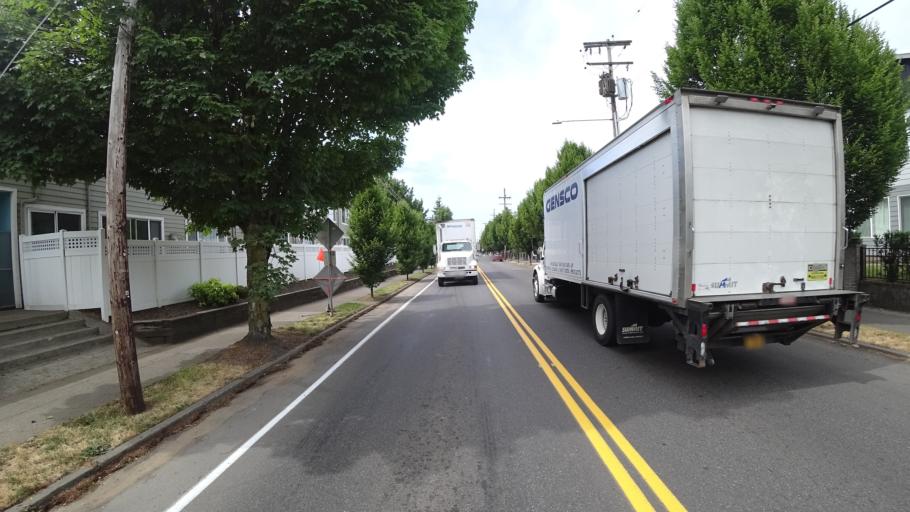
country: US
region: Oregon
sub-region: Washington County
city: West Haven
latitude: 45.5935
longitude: -122.7582
